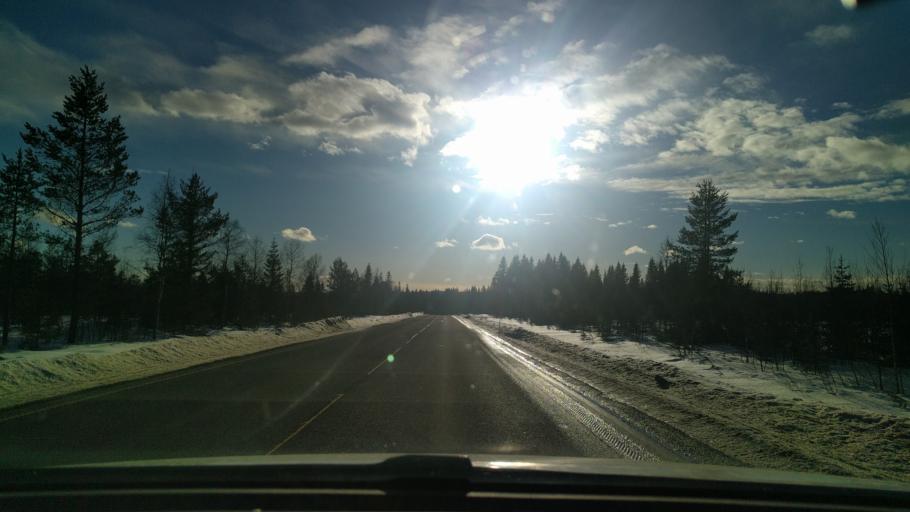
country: NO
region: Hedmark
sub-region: Trysil
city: Innbygda
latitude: 61.1180
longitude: 12.0565
